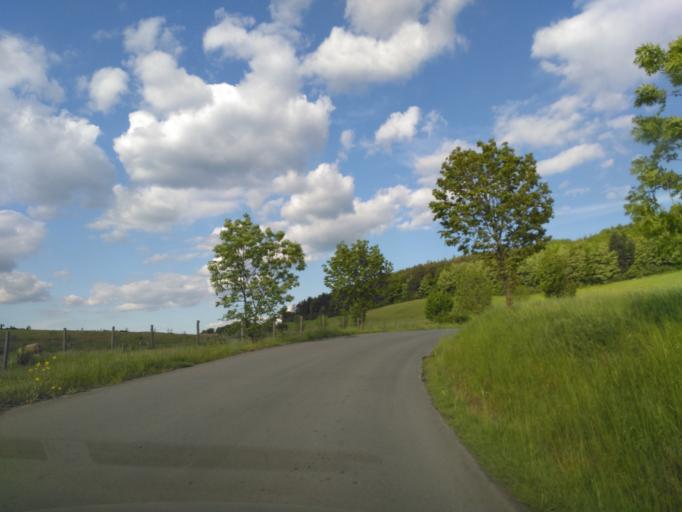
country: CZ
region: Central Bohemia
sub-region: Okres Beroun
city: Beroun
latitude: 49.9263
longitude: 14.0725
